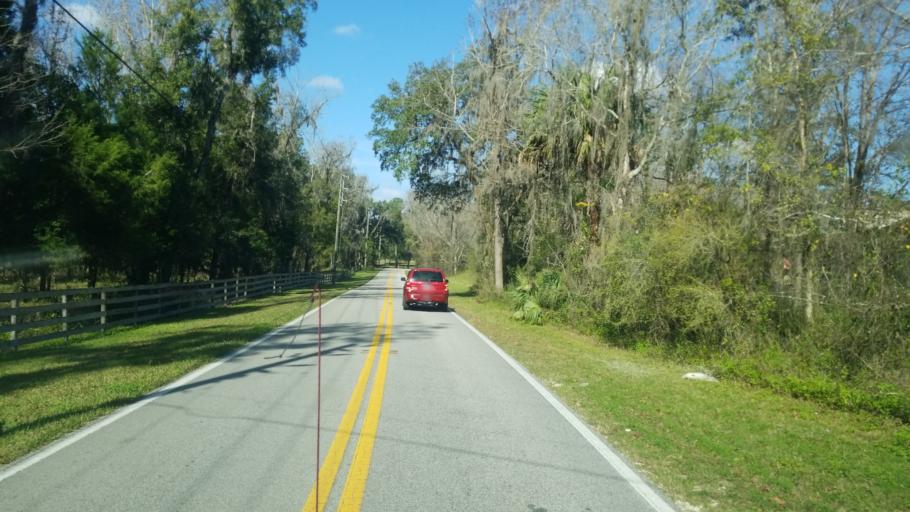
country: US
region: Florida
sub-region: Hernando County
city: North Brooksville
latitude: 28.5912
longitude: -82.3747
